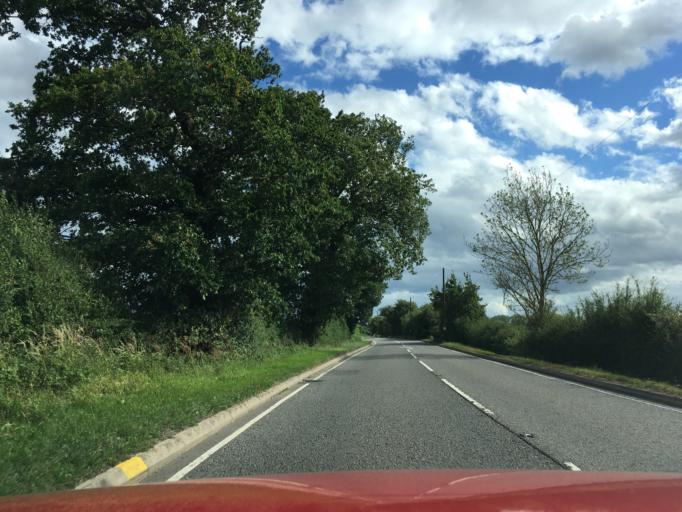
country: GB
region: England
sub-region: Warwickshire
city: Hartshill
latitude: 52.5649
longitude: -1.4823
